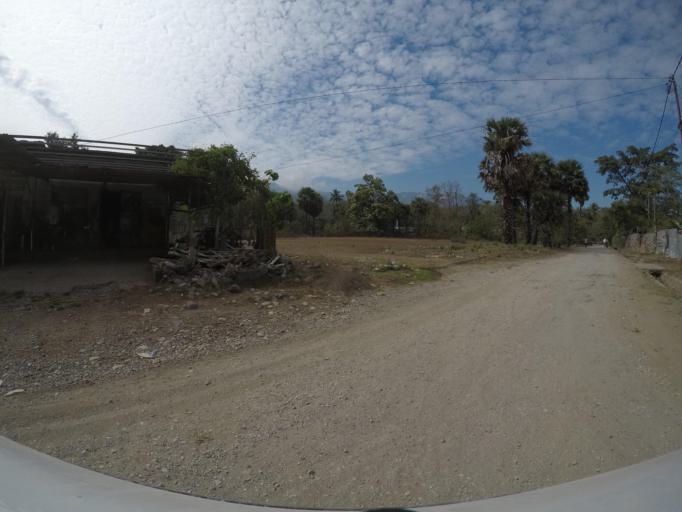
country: TL
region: Bobonaro
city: Maliana
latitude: -8.9911
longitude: 125.2217
